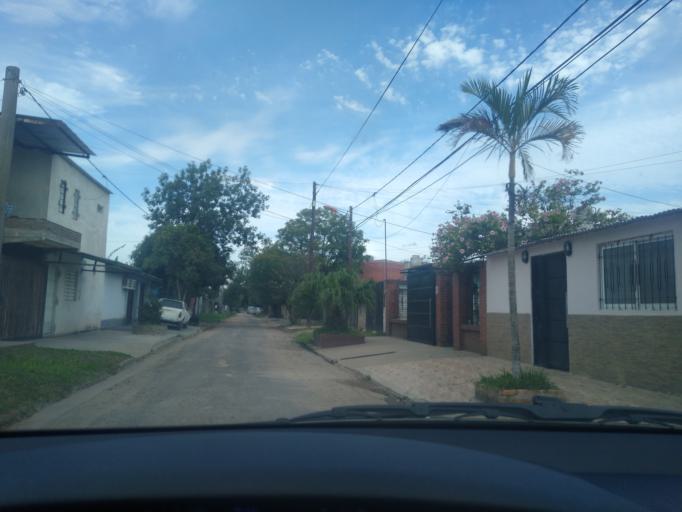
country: AR
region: Chaco
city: Resistencia
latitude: -27.4831
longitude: -58.9774
